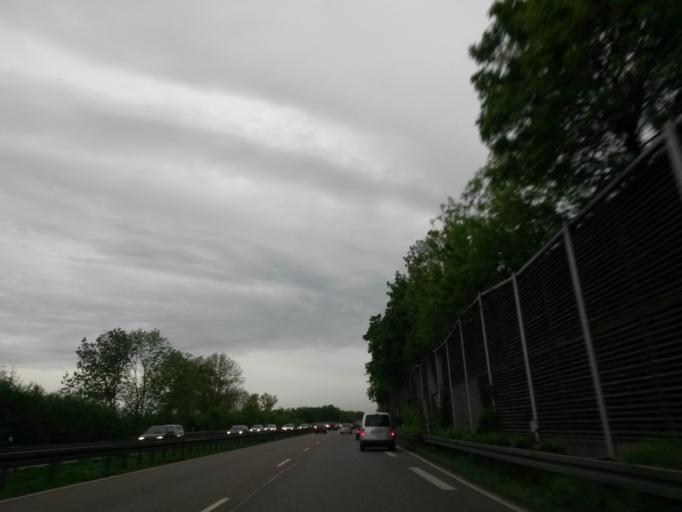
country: DE
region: Baden-Wuerttemberg
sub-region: Regierungsbezirk Stuttgart
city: Korntal
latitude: 48.8477
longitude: 9.1267
